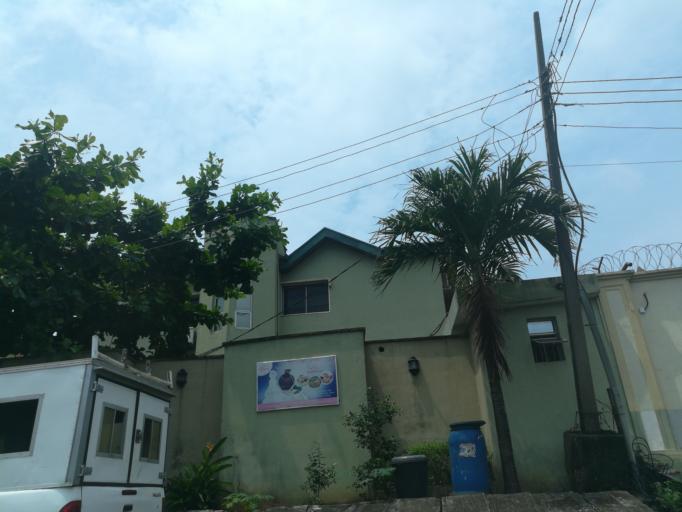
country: NG
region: Lagos
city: Ojota
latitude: 6.5904
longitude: 3.3642
